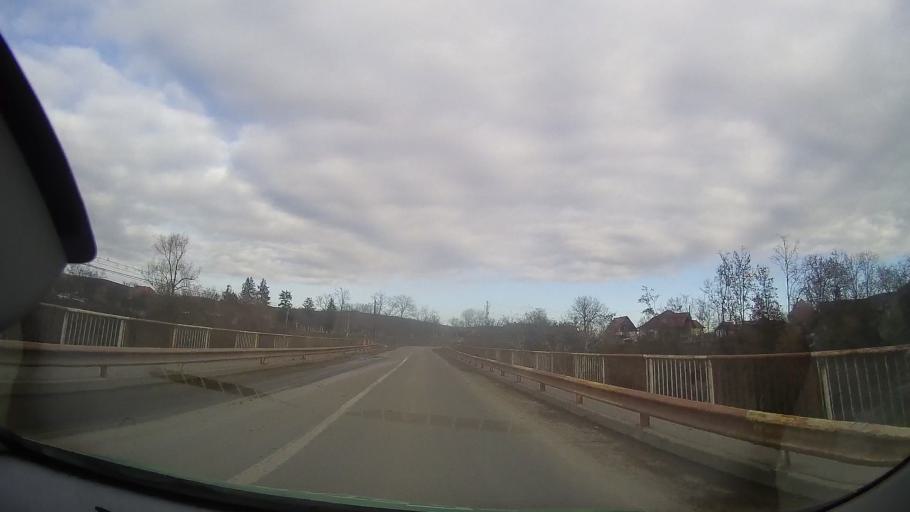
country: RO
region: Mures
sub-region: Comuna Iernut
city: Iernut
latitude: 46.4698
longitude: 24.2186
